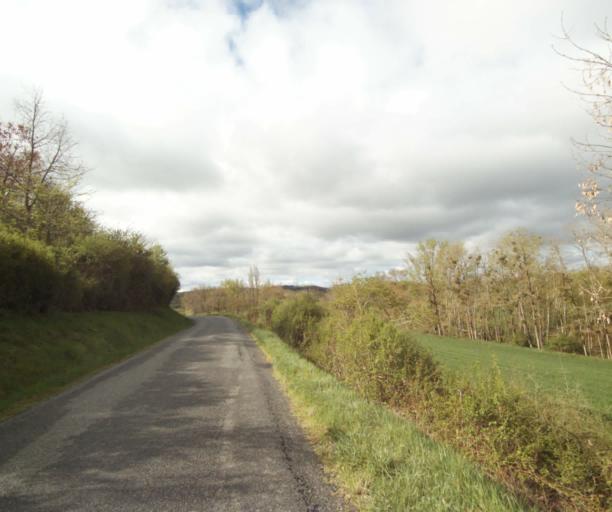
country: FR
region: Midi-Pyrenees
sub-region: Departement de l'Ariege
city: Saverdun
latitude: 43.2359
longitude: 1.5629
